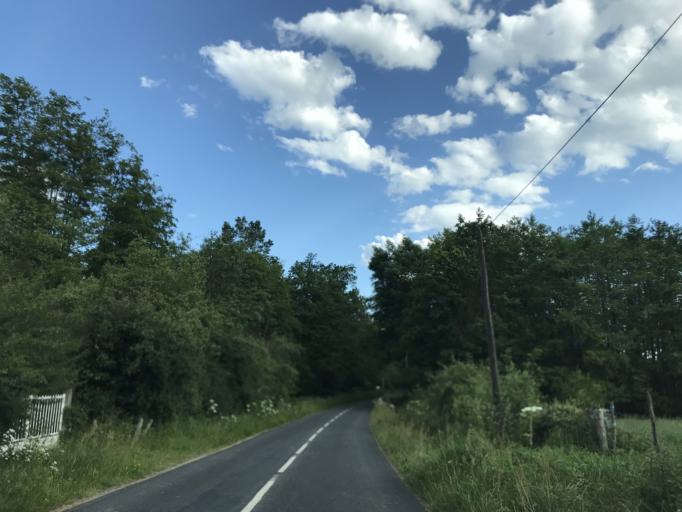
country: FR
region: Auvergne
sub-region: Departement du Puy-de-Dome
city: Courpiere
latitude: 45.7642
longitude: 3.6014
